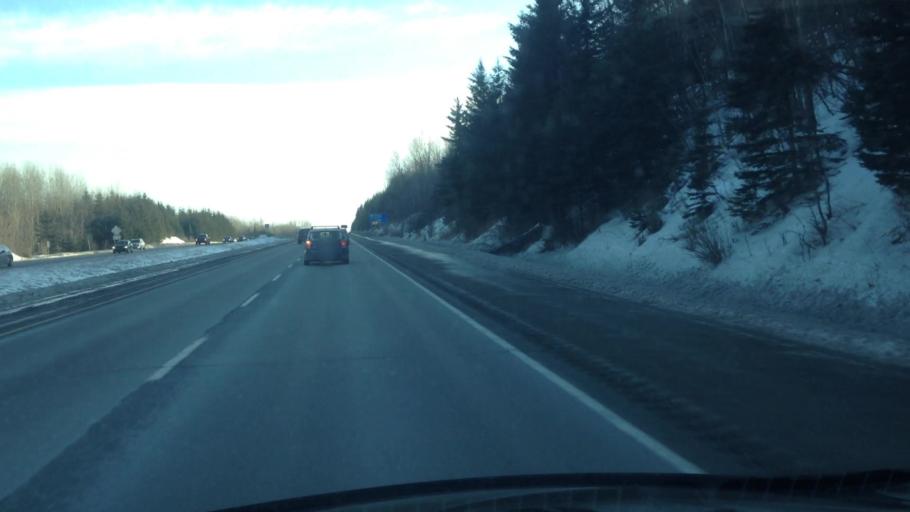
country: CA
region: Quebec
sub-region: Laurentides
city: Prevost
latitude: 45.8573
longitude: -74.0795
